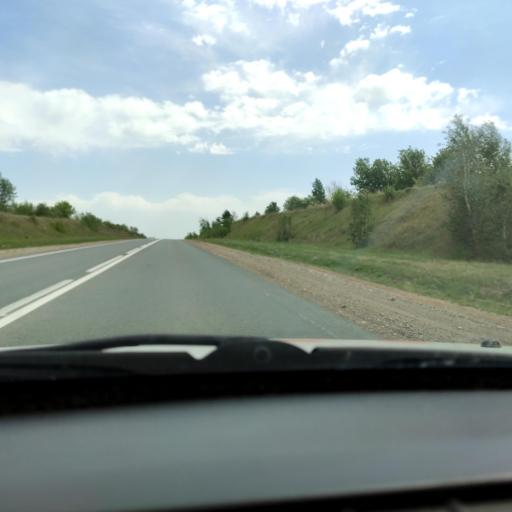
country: RU
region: Samara
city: Mirnyy
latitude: 53.6421
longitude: 50.2239
